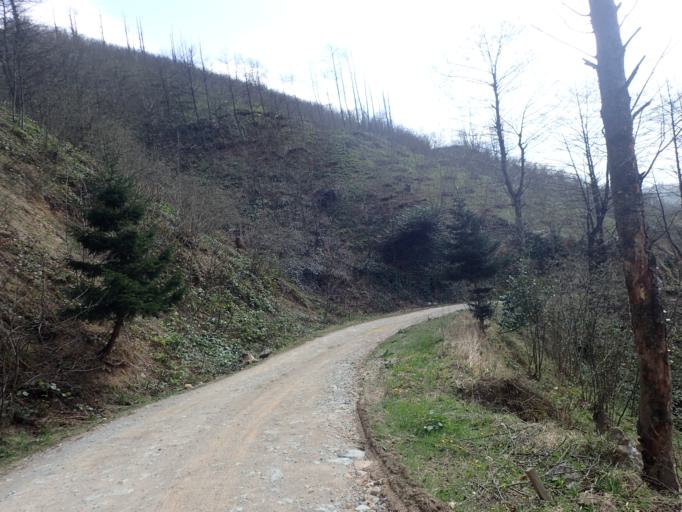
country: TR
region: Ordu
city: Kabaduz
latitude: 40.8188
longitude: 37.9033
